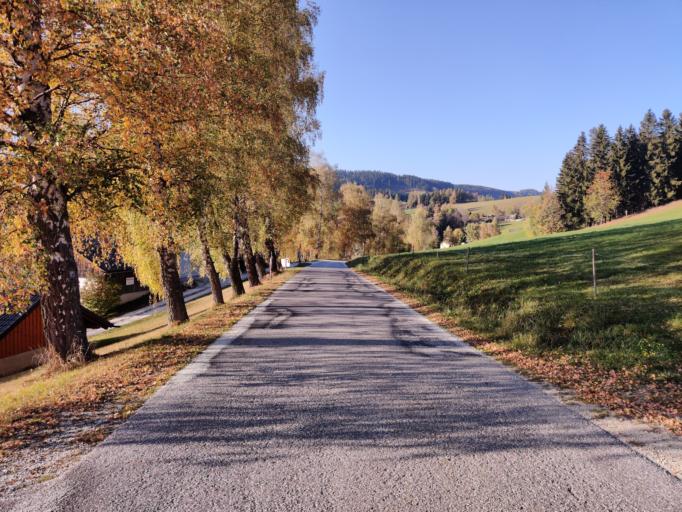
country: AT
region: Styria
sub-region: Politischer Bezirk Hartberg-Fuerstenfeld
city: Sankt Jakob im Walde
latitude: 47.4702
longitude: 15.7981
